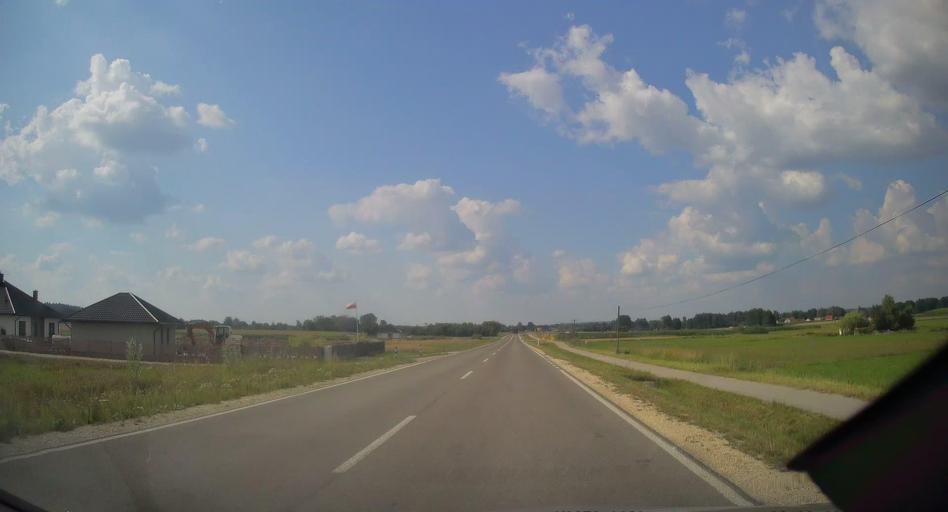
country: PL
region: Swietokrzyskie
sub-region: Powiat kielecki
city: Lopuszno
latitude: 50.9581
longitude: 20.2491
